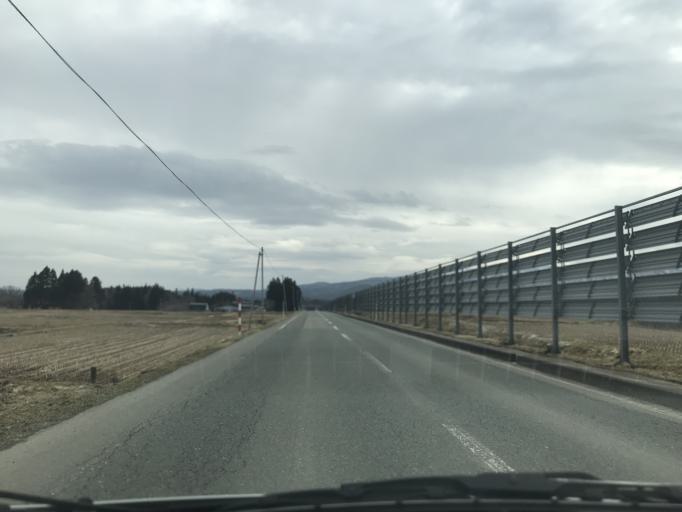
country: JP
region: Iwate
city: Hanamaki
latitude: 39.3362
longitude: 140.9755
